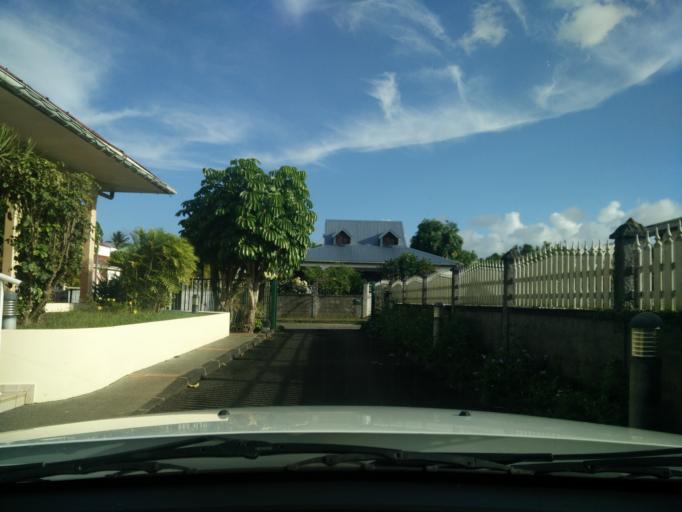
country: GP
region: Guadeloupe
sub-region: Guadeloupe
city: Baie-Mahault
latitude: 16.2590
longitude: -61.5814
